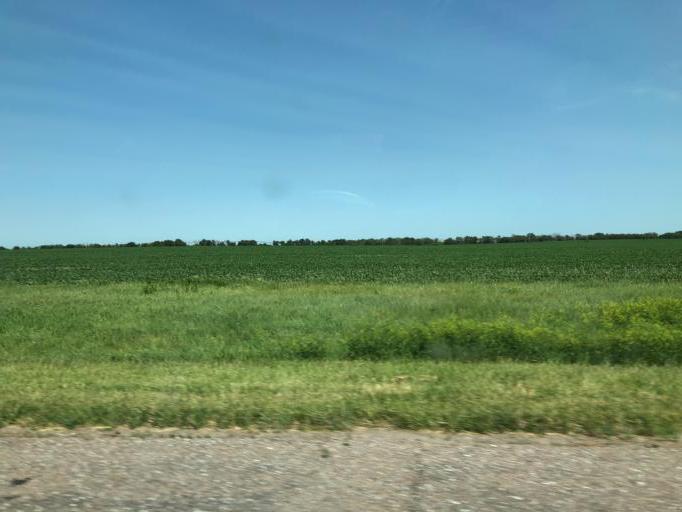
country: US
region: Nebraska
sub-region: Thayer County
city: Hebron
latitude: 40.2868
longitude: -97.5765
